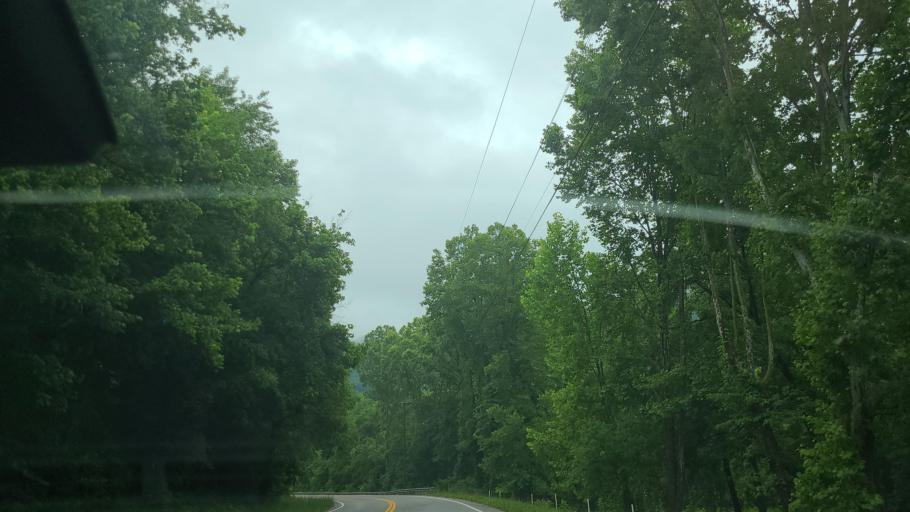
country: US
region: Tennessee
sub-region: Anderson County
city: Oak Ridge
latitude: 36.0913
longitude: -84.2708
